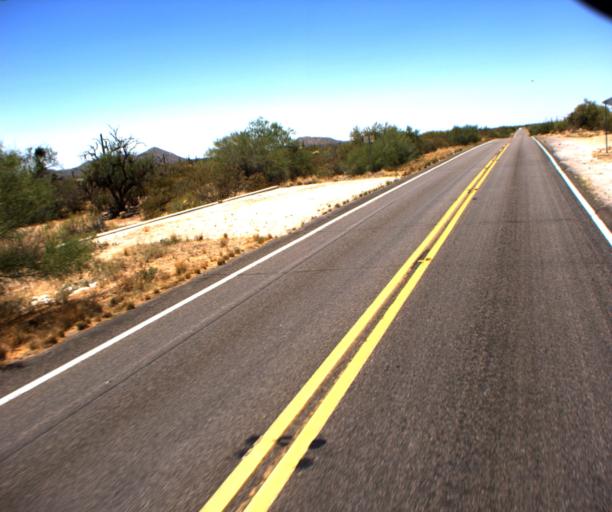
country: US
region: Arizona
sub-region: Pima County
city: Catalina
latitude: 32.7077
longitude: -111.0979
